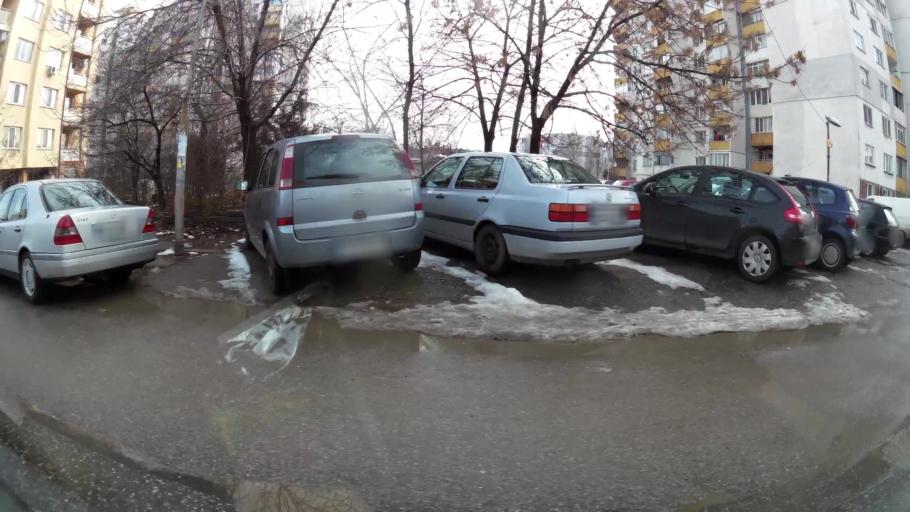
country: BG
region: Sofia-Capital
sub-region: Stolichna Obshtina
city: Sofia
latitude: 42.7131
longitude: 23.2712
